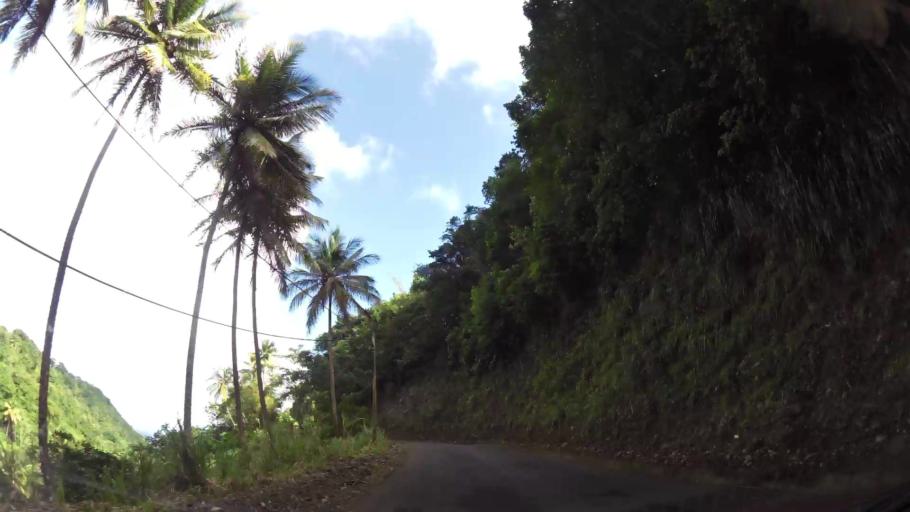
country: DM
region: Saint John
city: Portsmouth
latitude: 15.6198
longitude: -61.4177
